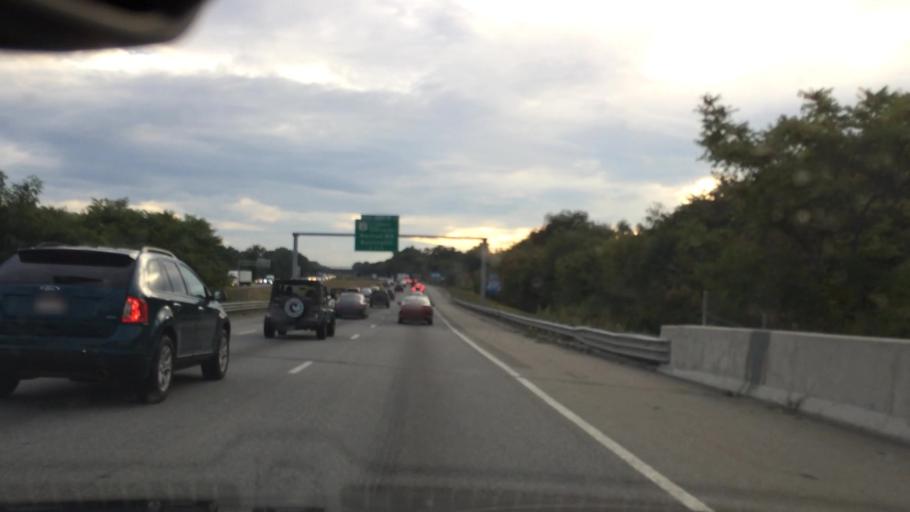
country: US
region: Massachusetts
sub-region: Middlesex County
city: Lowell
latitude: 42.6165
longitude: -71.2958
